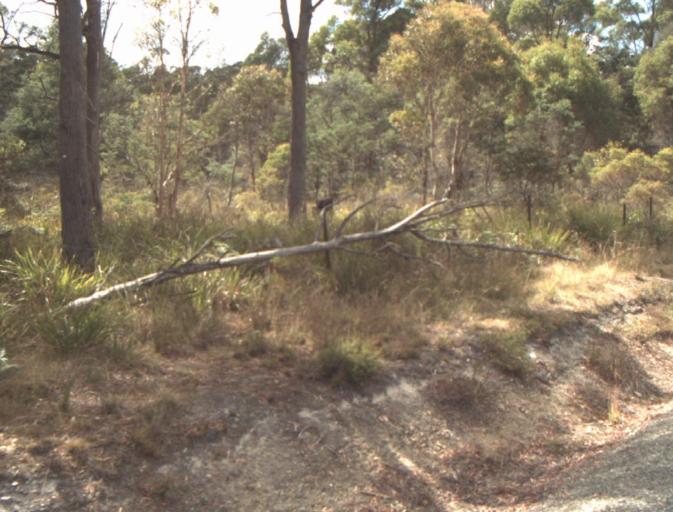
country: AU
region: Tasmania
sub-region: Launceston
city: Mayfield
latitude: -41.2095
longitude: 147.1308
